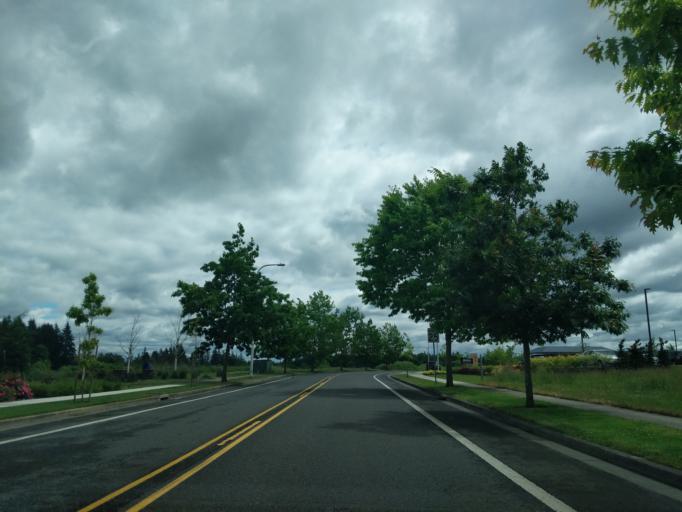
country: US
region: Oregon
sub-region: Yamhill County
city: Newberg
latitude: 45.3068
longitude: -122.9340
